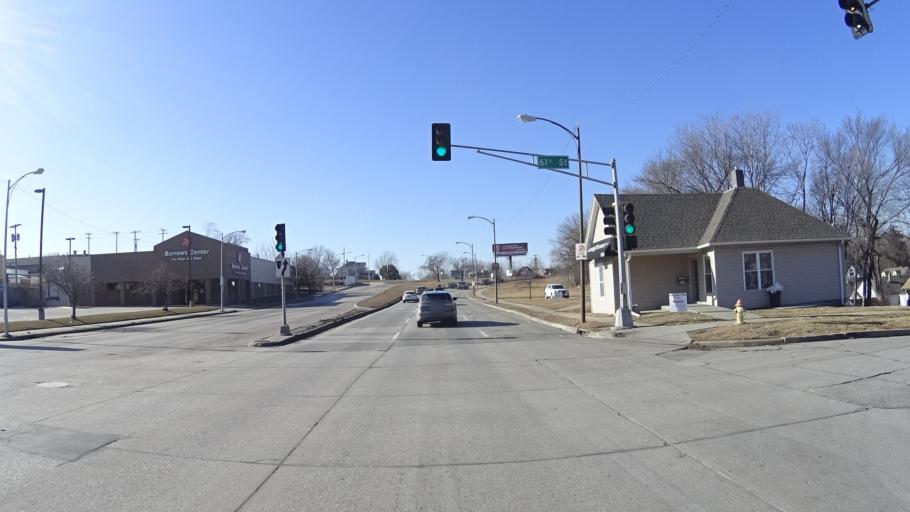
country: US
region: Nebraska
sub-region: Douglas County
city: Omaha
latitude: 41.2869
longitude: -96.0070
